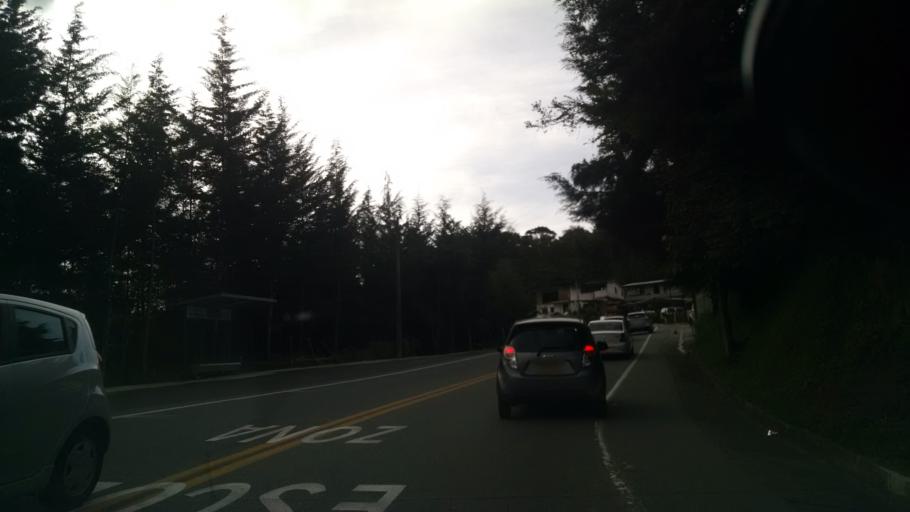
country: CO
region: Antioquia
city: El Retiro
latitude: 6.1344
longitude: -75.5086
